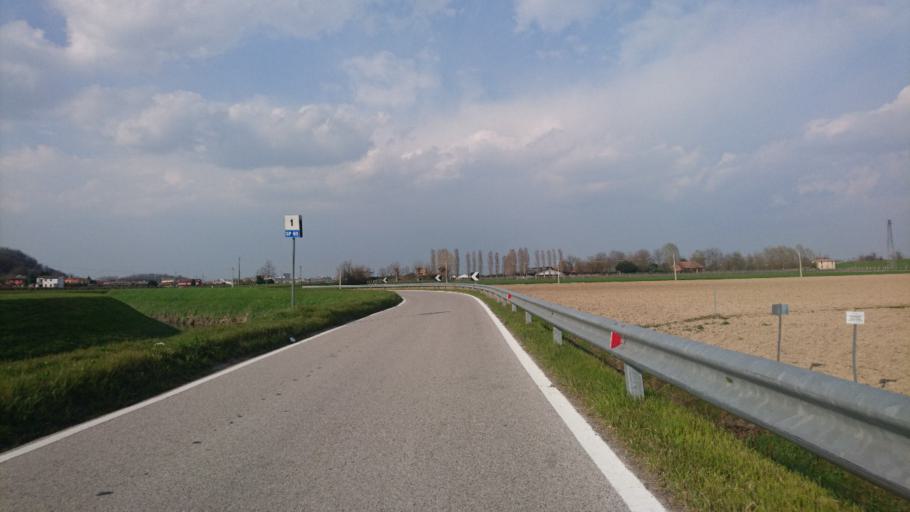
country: IT
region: Veneto
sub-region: Provincia di Padova
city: Battaglia Terme
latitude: 45.3036
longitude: 11.7918
